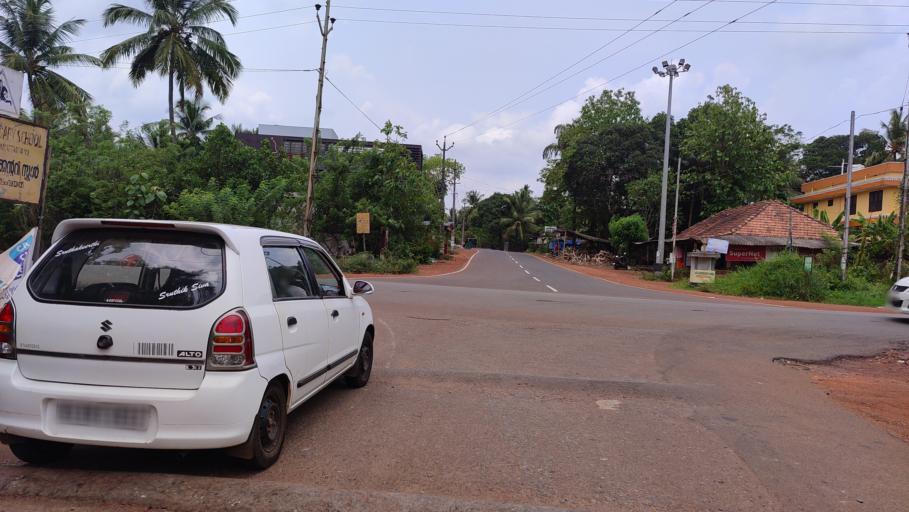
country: IN
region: Kerala
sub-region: Kasaragod District
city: Kannangad
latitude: 12.3207
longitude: 75.1070
